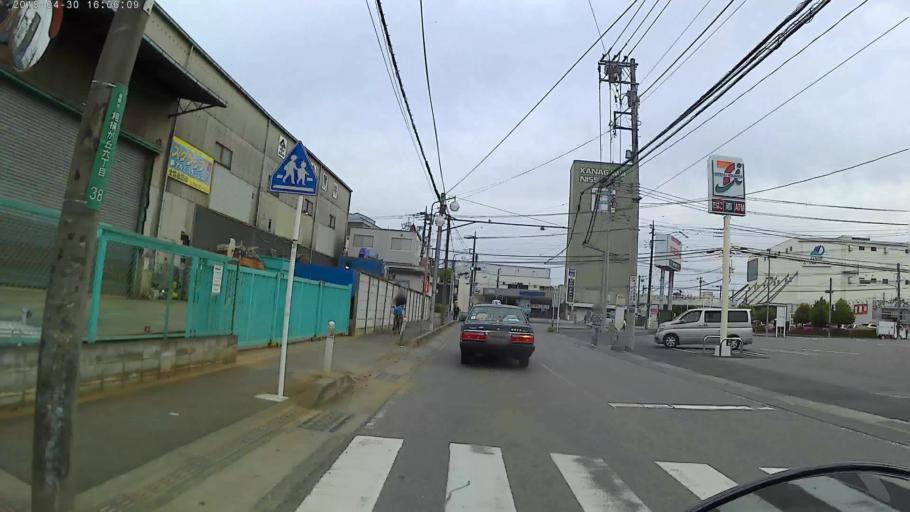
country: JP
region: Kanagawa
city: Minami-rinkan
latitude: 35.5023
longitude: 139.4282
